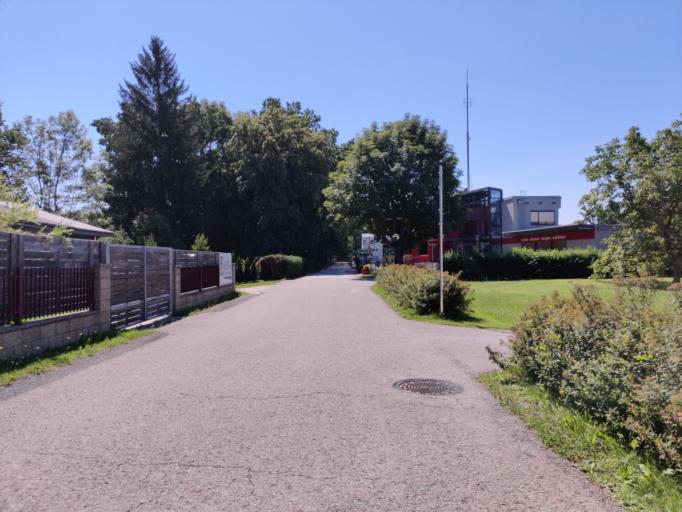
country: AT
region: Styria
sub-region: Politischer Bezirk Leibnitz
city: Stocking
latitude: 46.8523
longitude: 15.5399
